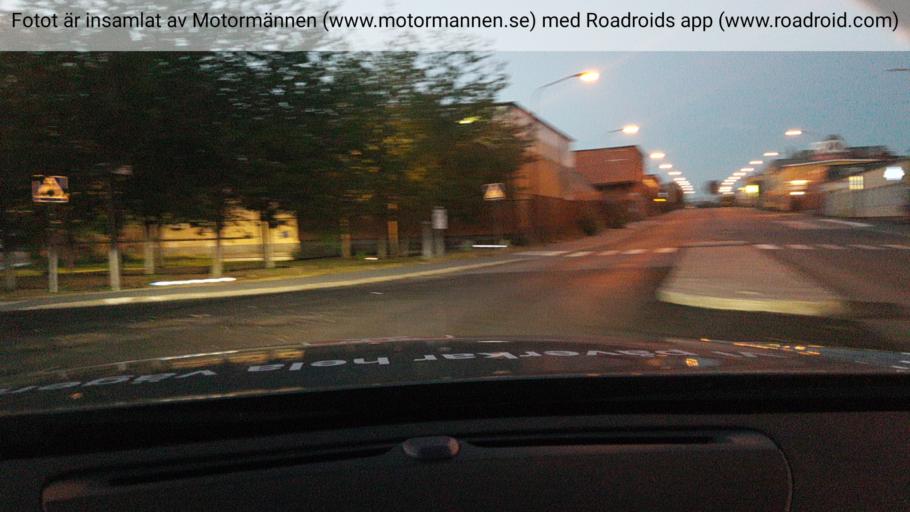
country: SE
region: Stockholm
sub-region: Stockholms Kommun
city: Arsta
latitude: 59.2594
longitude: 18.0520
